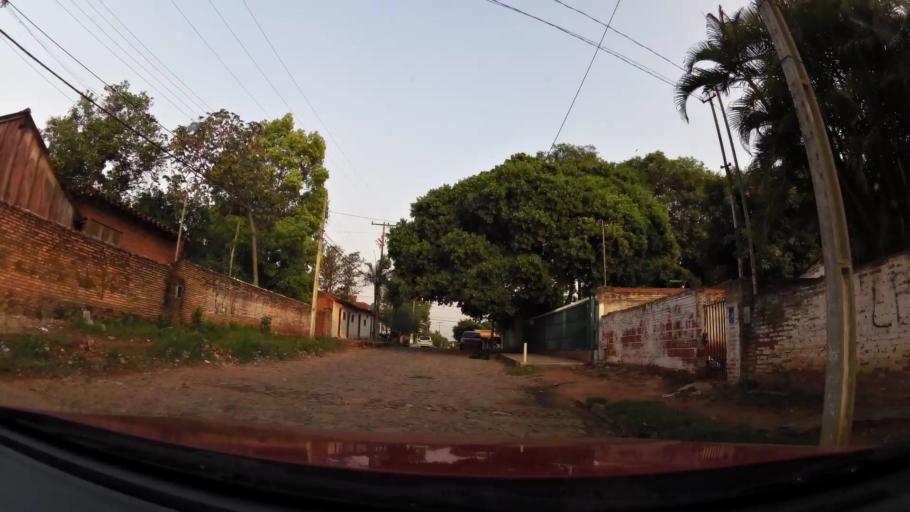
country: PY
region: Central
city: Lambare
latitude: -25.3540
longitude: -57.5977
